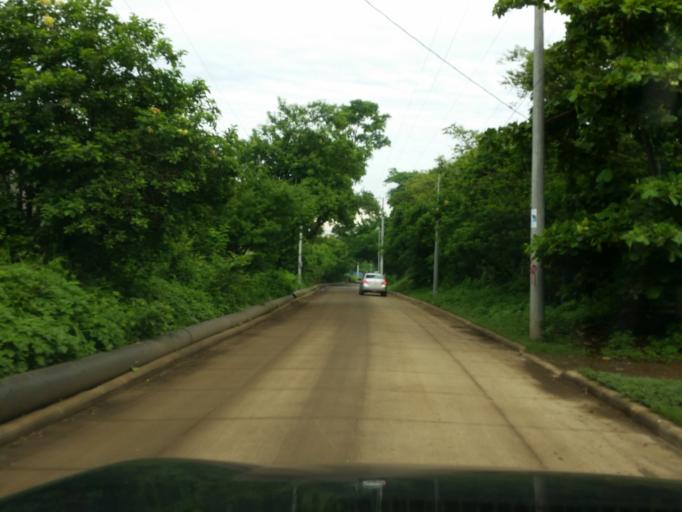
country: NI
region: Managua
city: Managua
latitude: 12.0982
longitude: -86.2118
